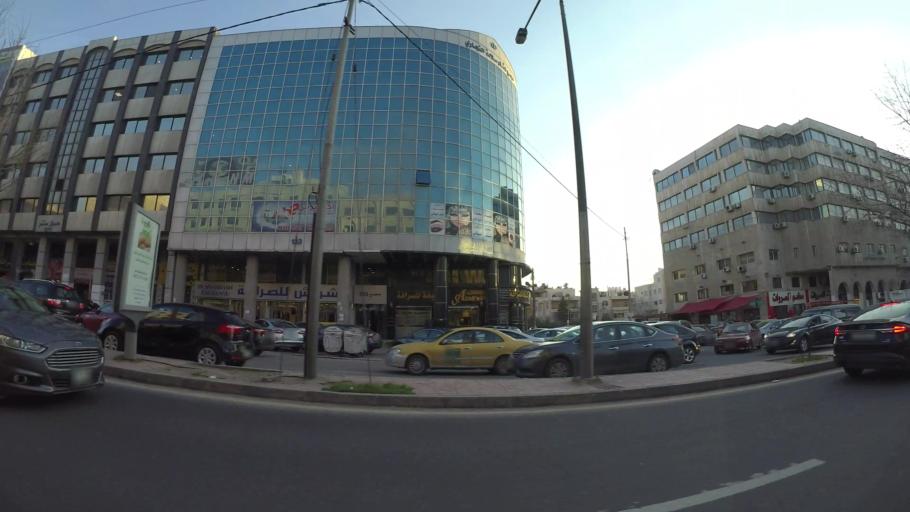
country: JO
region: Amman
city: Al Jubayhah
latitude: 31.9896
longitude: 35.8726
